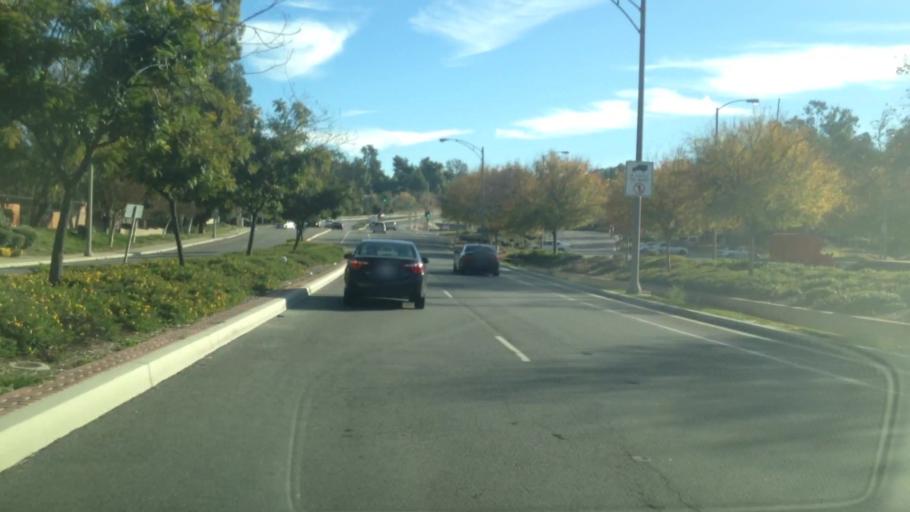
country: US
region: California
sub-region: Riverside County
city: Riverside
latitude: 33.9575
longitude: -117.3470
